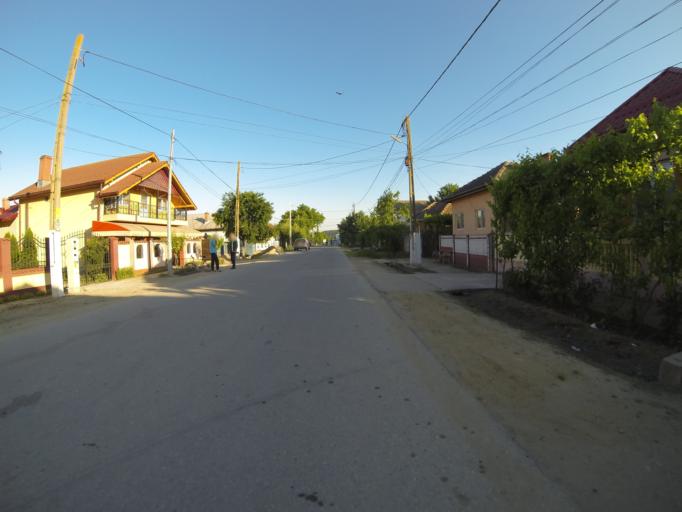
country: RO
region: Dolj
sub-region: Comuna Tuglui
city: Tuglui
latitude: 44.1885
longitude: 23.8120
